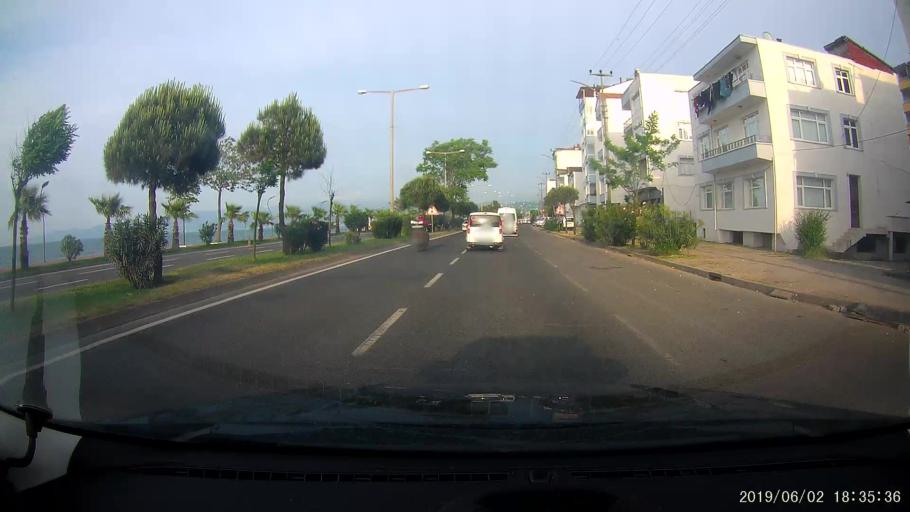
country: TR
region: Ordu
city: Fatsa
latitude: 41.0261
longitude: 37.5183
